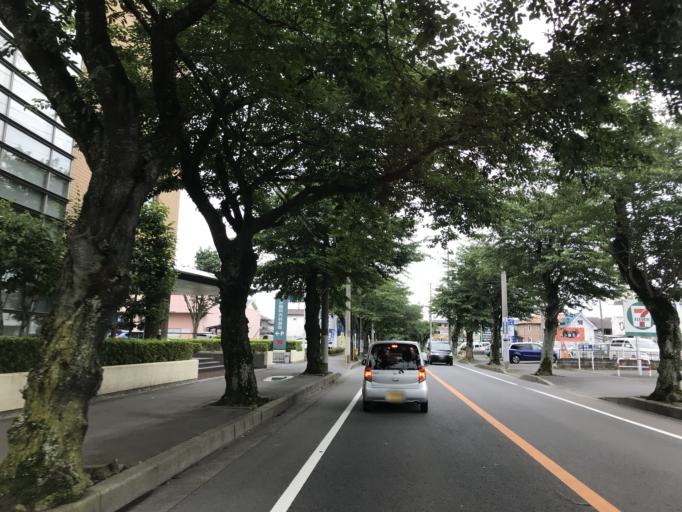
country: JP
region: Ibaraki
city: Mito-shi
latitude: 36.3318
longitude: 140.4598
